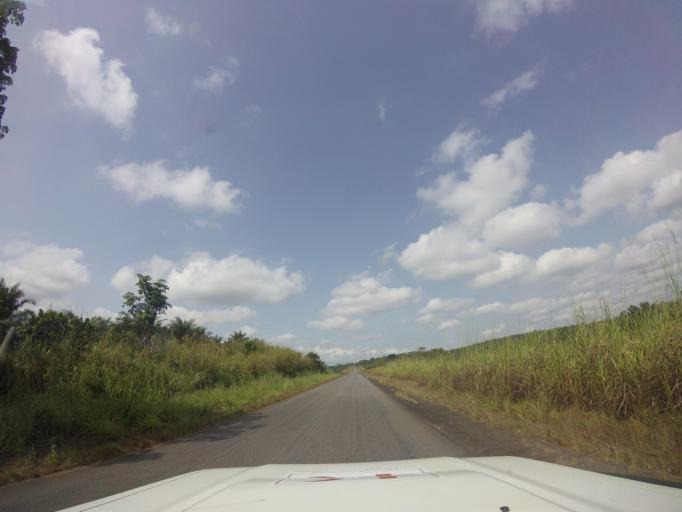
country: LR
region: Bomi
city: Tubmanburg
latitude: 6.7223
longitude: -11.0529
